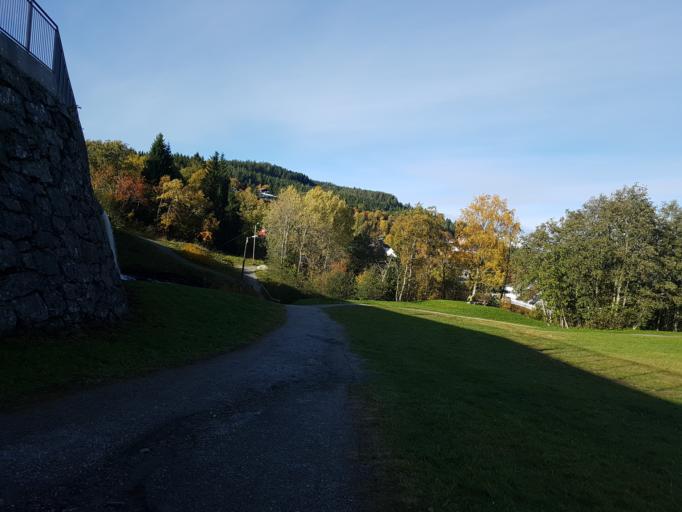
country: NO
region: Sor-Trondelag
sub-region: Trondheim
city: Trondheim
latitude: 63.4231
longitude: 10.3490
